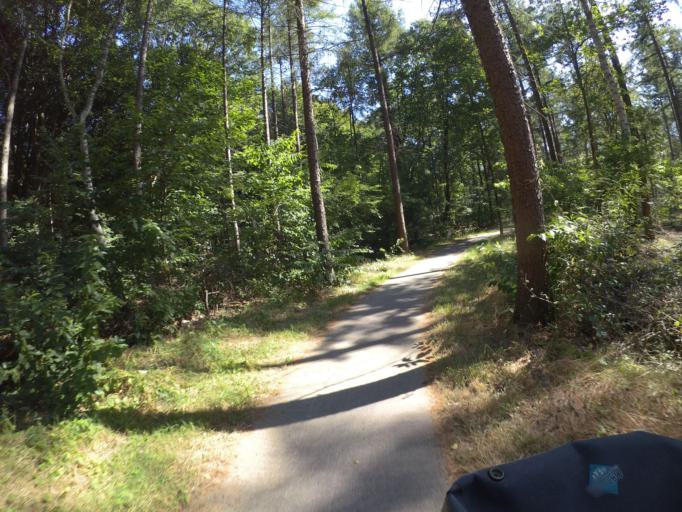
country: NL
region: Friesland
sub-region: Gemeente Gaasterlan-Sleat
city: Oudemirdum
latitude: 52.8630
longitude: 5.5508
